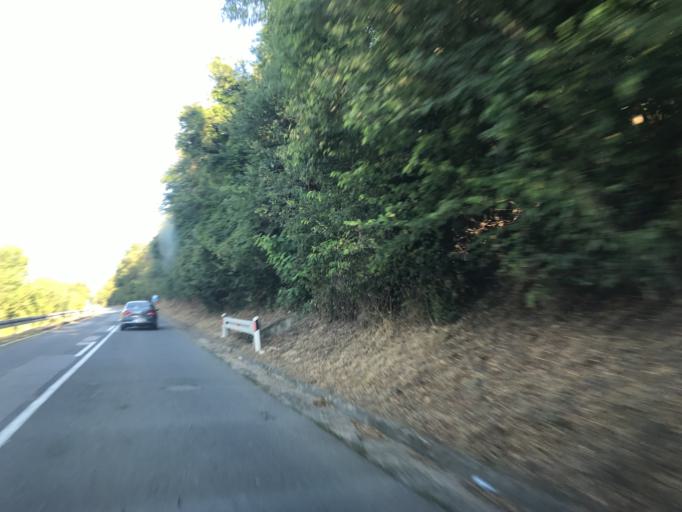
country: RO
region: Mehedinti
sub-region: Comuna Svinita
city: Svinita
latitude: 44.4726
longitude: 22.1143
